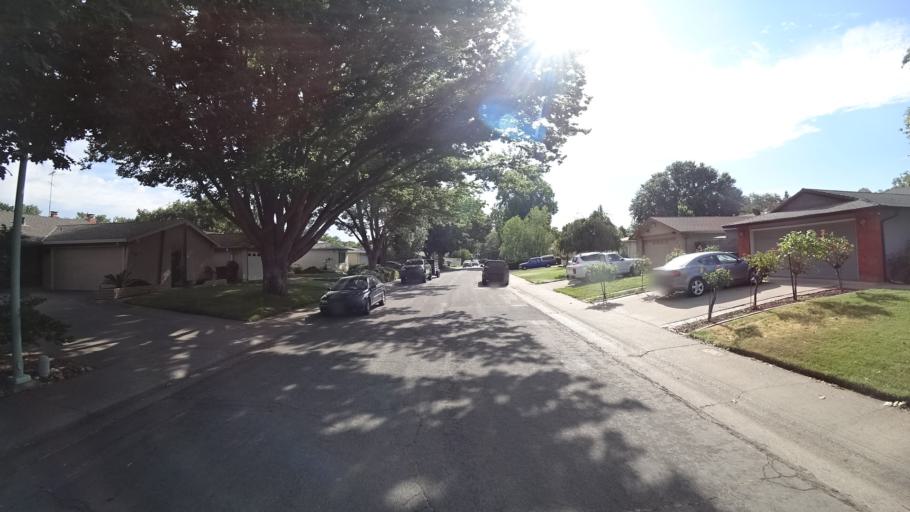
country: US
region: California
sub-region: Sacramento County
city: Rosemont
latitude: 38.5634
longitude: -121.3886
